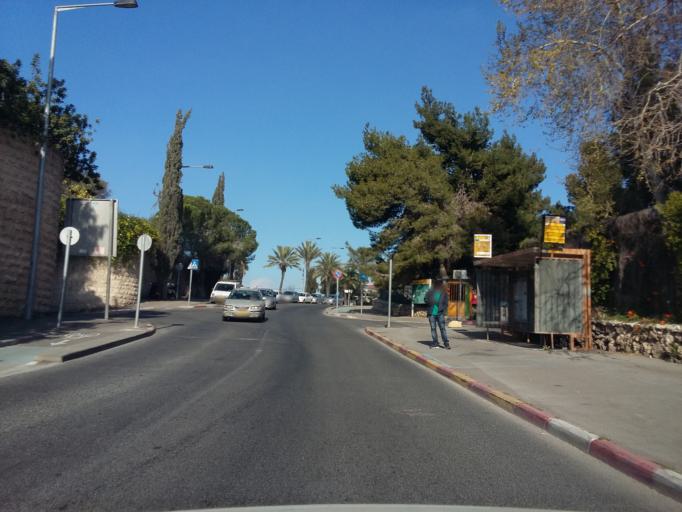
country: PS
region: West Bank
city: East Jerusalem
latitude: 31.7983
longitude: 35.2372
